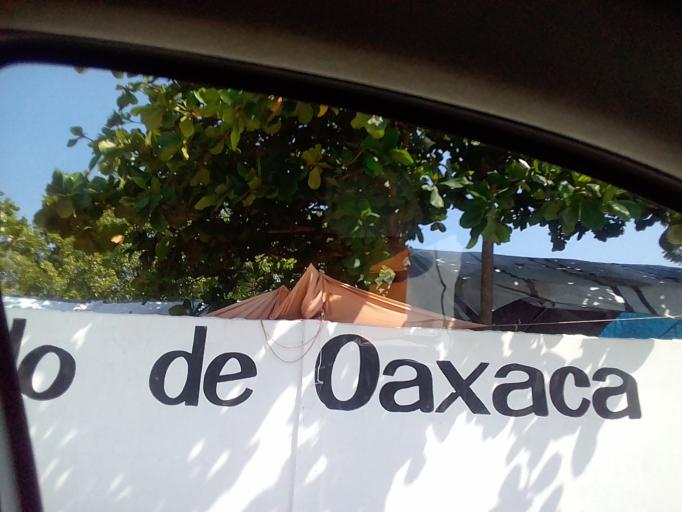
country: MX
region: Oaxaca
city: San Francisco Ixhuatan
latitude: 16.3575
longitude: -94.4810
